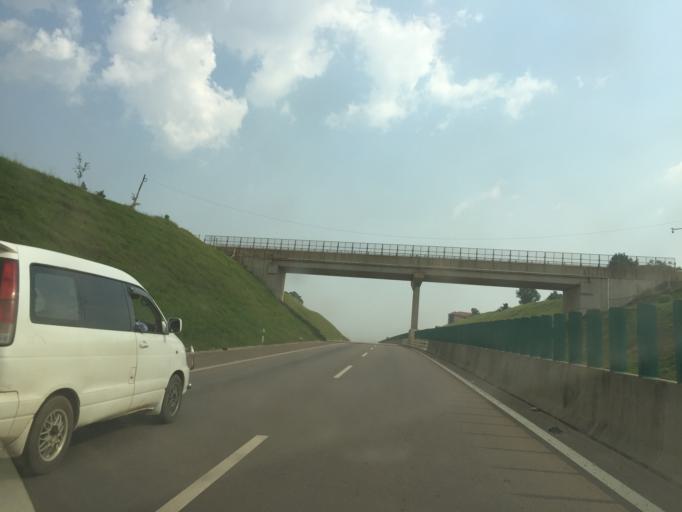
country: UG
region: Central Region
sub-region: Wakiso District
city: Kajansi
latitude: 0.2823
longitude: 32.5129
